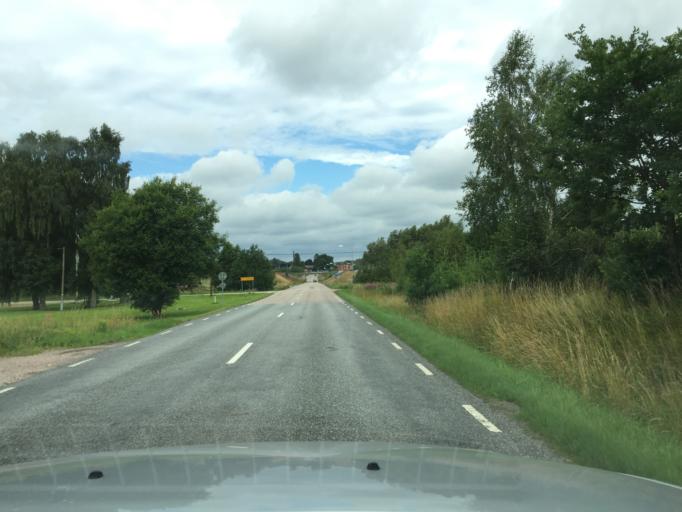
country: SE
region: Skane
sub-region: Hassleholms Kommun
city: Sosdala
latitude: 56.0289
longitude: 13.6872
